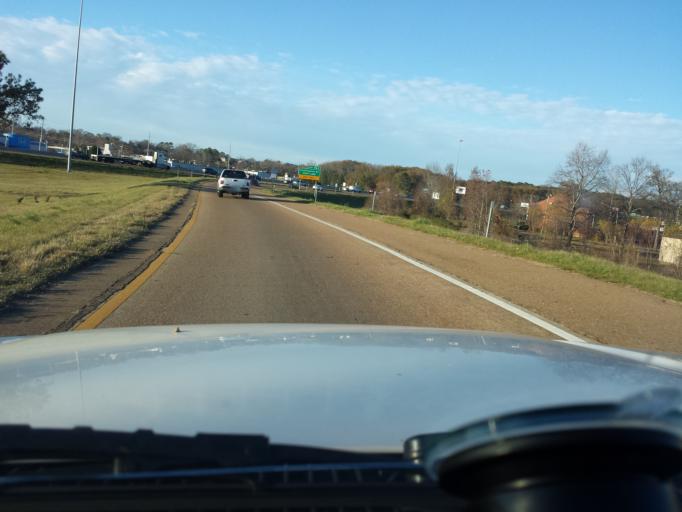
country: US
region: Mississippi
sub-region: Hinds County
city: Jackson
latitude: 32.3045
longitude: -90.1642
